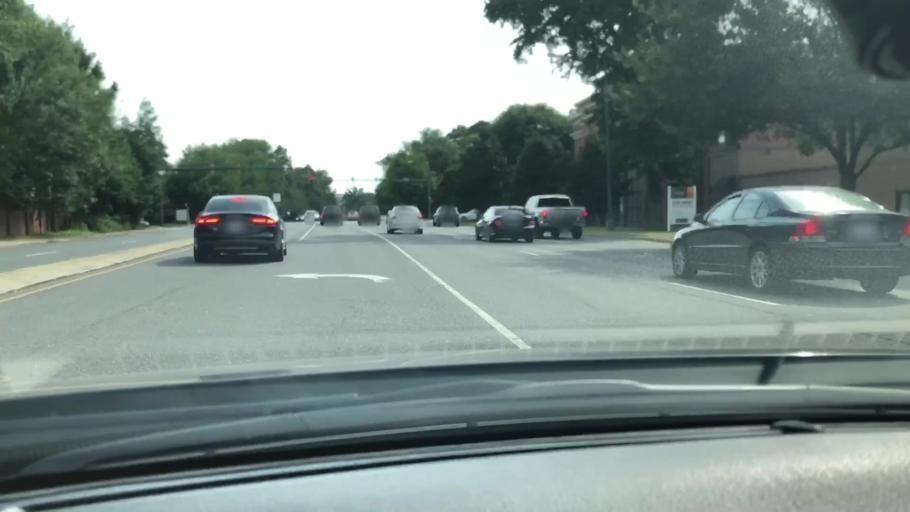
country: US
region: North Carolina
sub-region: Mecklenburg County
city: Charlotte
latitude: 35.1557
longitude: -80.8238
